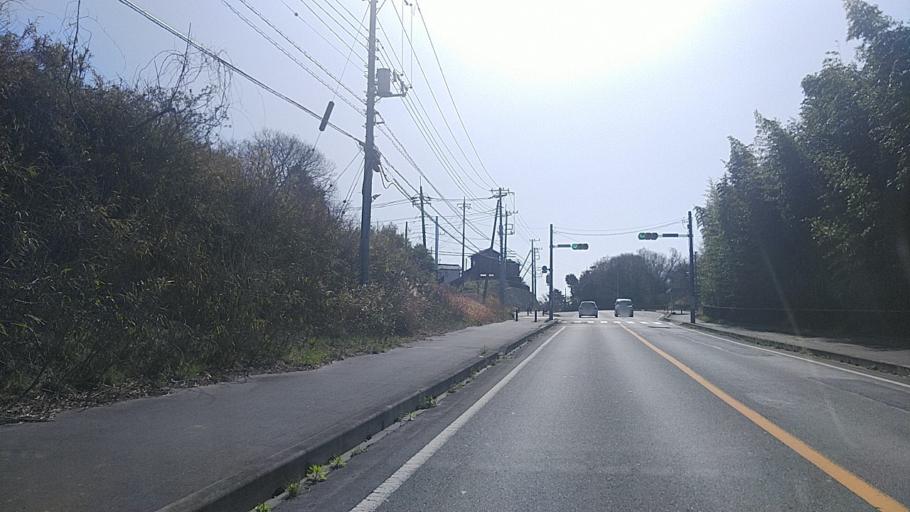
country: JP
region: Ibaraki
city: Toride
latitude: 35.8894
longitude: 140.0987
